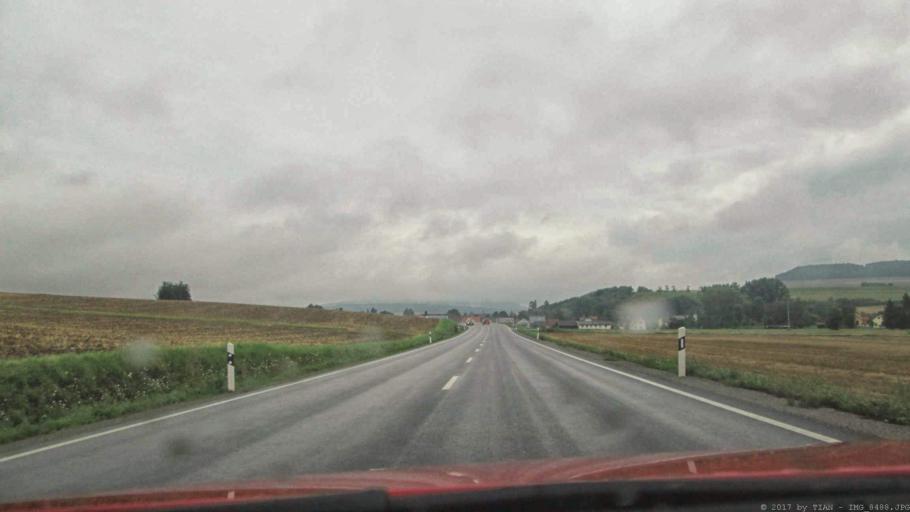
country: DE
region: Bavaria
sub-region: Regierungsbezirk Unterfranken
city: Karsbach
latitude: 50.0616
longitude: 9.7913
